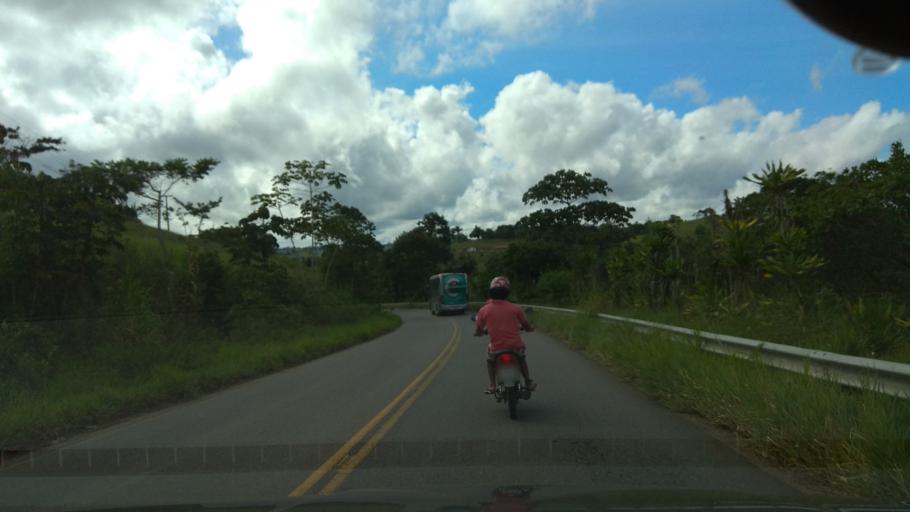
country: BR
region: Bahia
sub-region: Mutuipe
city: Mutuipe
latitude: -13.2127
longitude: -39.4775
